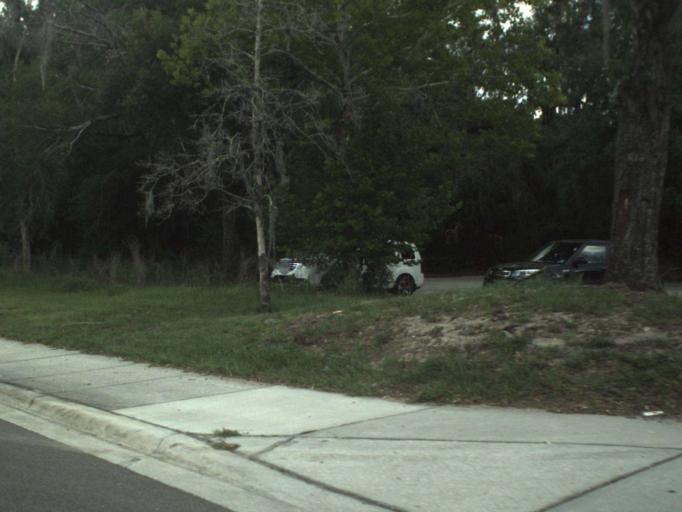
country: US
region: Florida
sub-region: Seminole County
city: Wekiwa Springs
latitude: 28.6876
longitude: -81.3943
